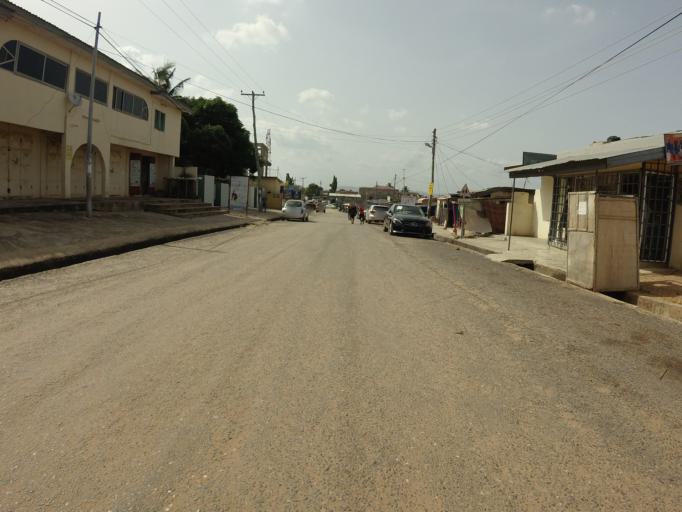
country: GH
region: Greater Accra
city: Dome
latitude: 5.6119
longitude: -0.2397
